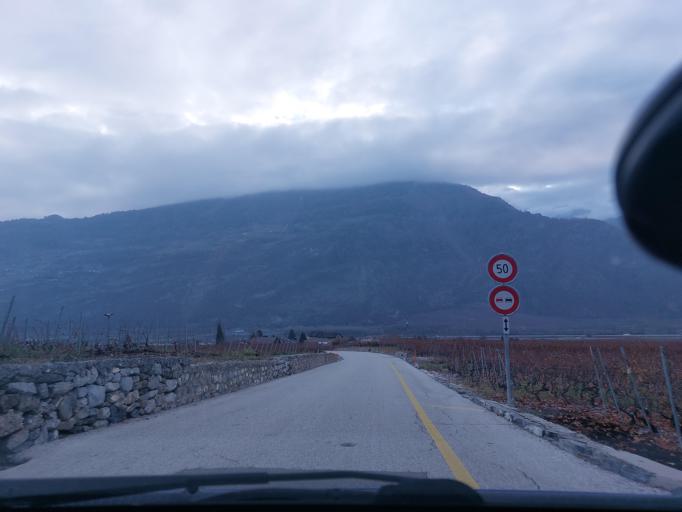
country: CH
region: Valais
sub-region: Conthey District
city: Chamoson
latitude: 46.1968
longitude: 7.2287
